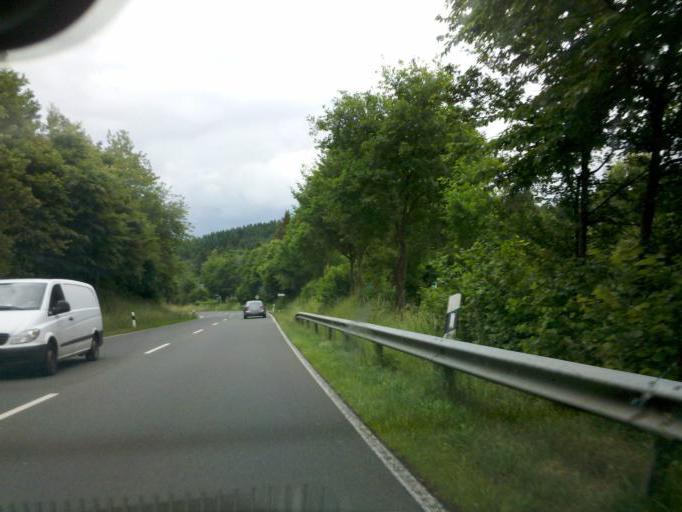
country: DE
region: North Rhine-Westphalia
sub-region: Regierungsbezirk Arnsberg
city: Olpe
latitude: 51.0456
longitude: 7.8609
